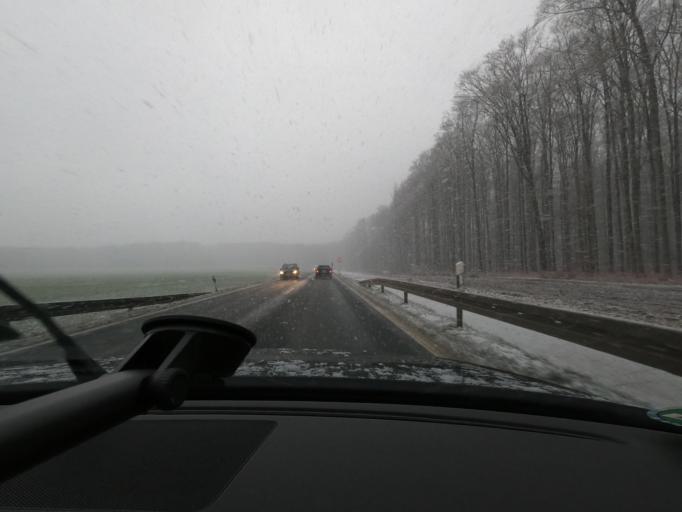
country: DE
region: Thuringia
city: Kallmerode
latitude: 51.3377
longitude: 10.3159
